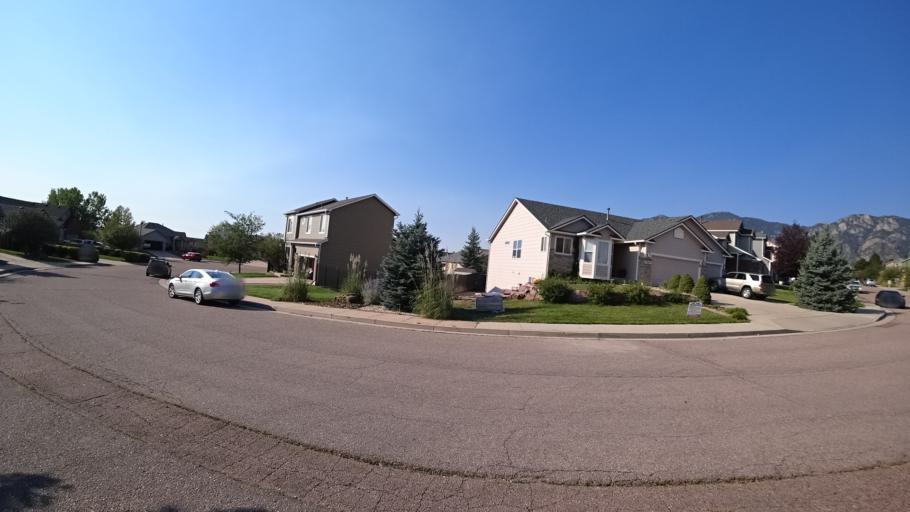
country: US
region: Colorado
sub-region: El Paso County
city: Stratmoor
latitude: 38.7707
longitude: -104.8081
